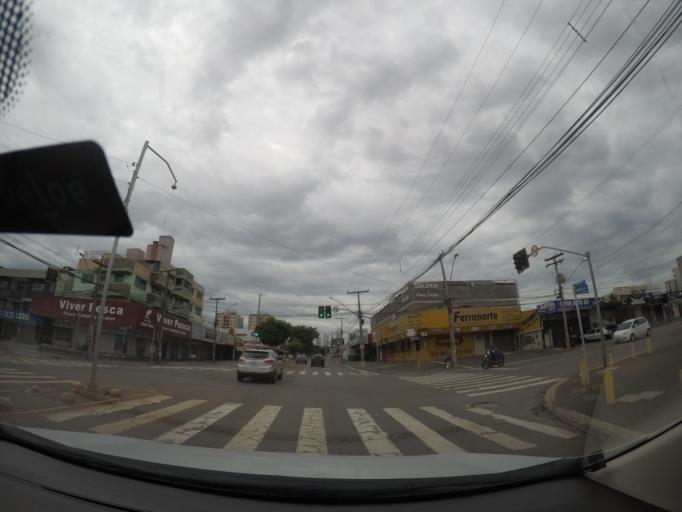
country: BR
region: Goias
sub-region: Goiania
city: Goiania
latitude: -16.7105
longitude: -49.2891
